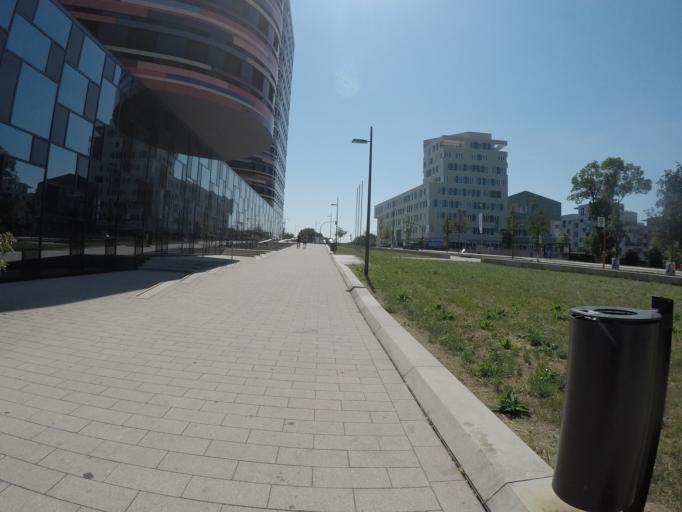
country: DE
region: Hamburg
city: Kleiner Grasbrook
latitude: 53.4980
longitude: 10.0030
